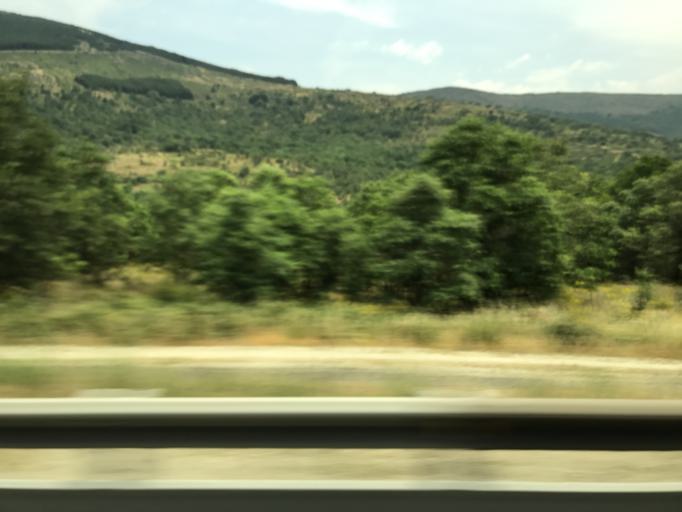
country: ES
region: Madrid
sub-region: Provincia de Madrid
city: Robregordo
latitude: 41.0996
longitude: -3.5917
